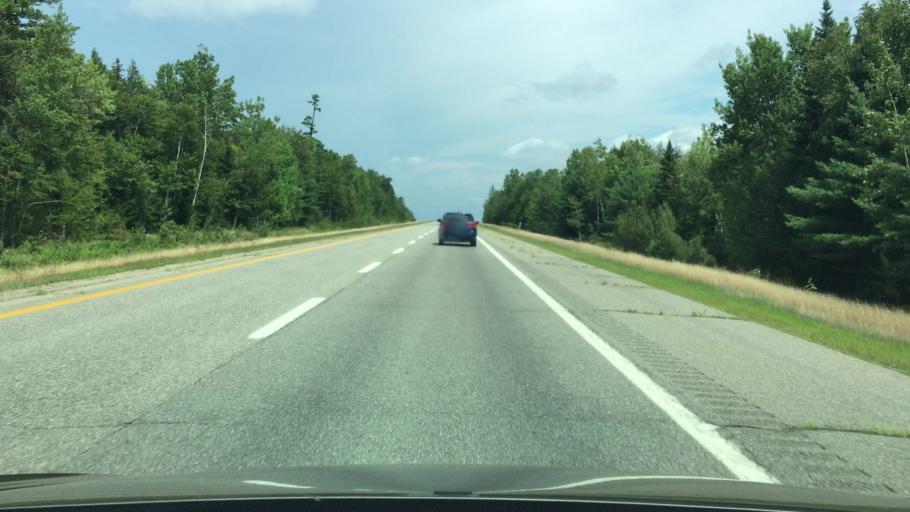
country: US
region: Maine
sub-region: Penobscot County
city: Howland
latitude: 45.2772
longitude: -68.6735
